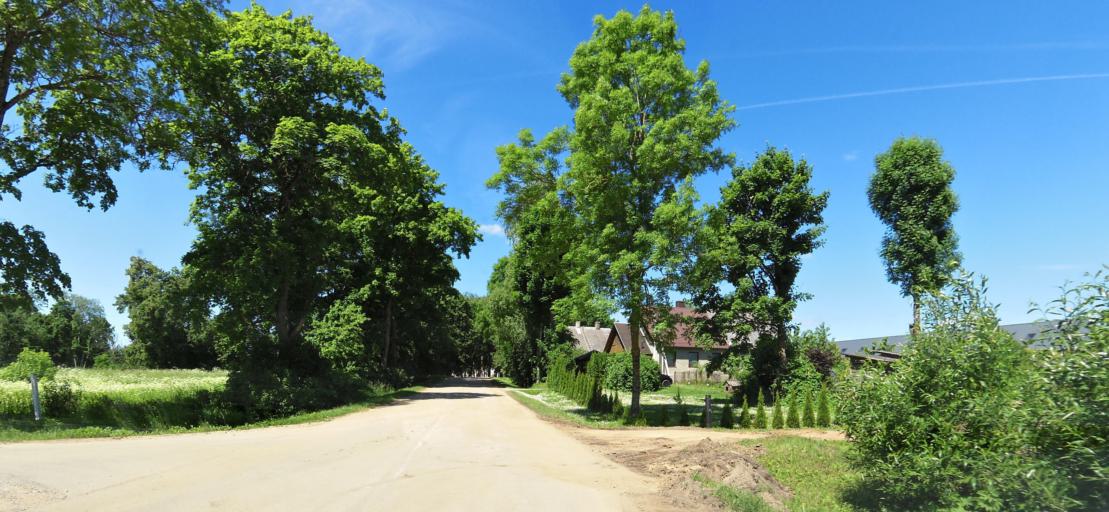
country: LT
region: Vilnius County
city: Pasilaiciai
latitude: 54.9844
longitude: 25.2261
